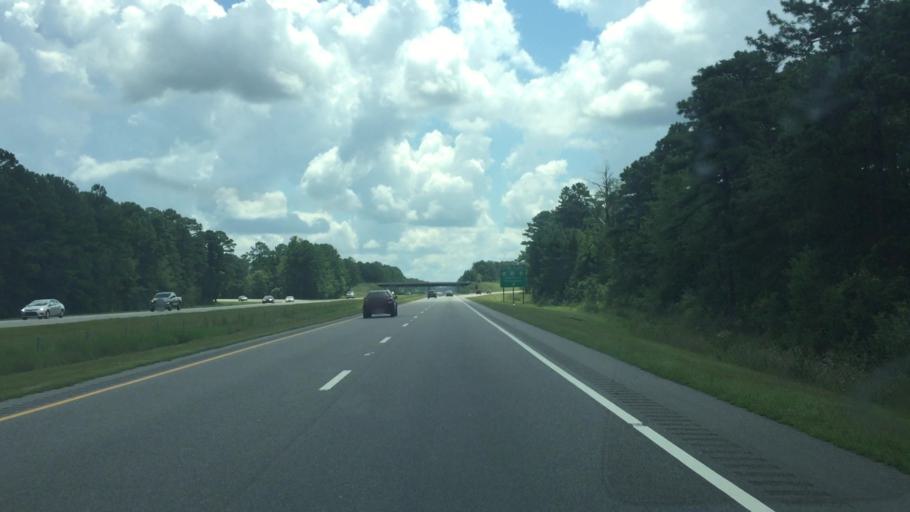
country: US
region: North Carolina
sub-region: Columbus County
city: Chadbourn
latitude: 34.3645
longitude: -78.8349
